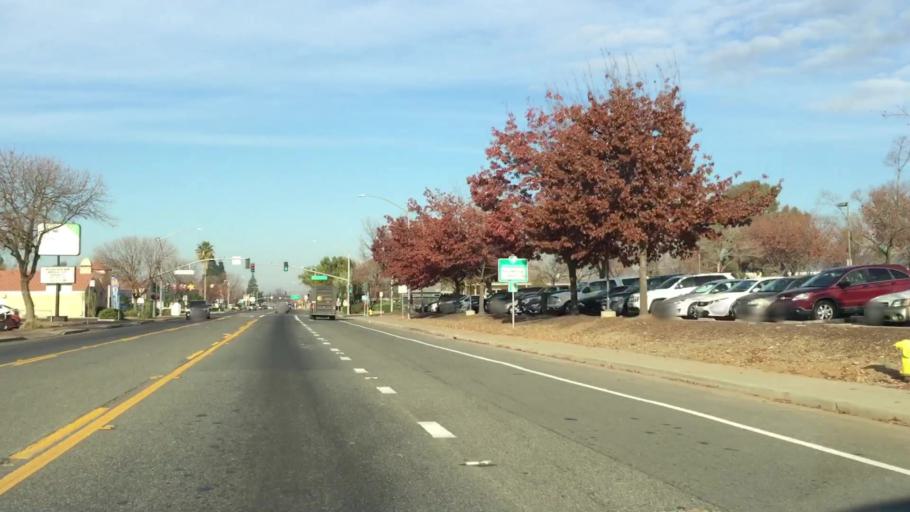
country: US
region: California
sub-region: Butte County
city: South Oroville
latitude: 39.5036
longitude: -121.5405
